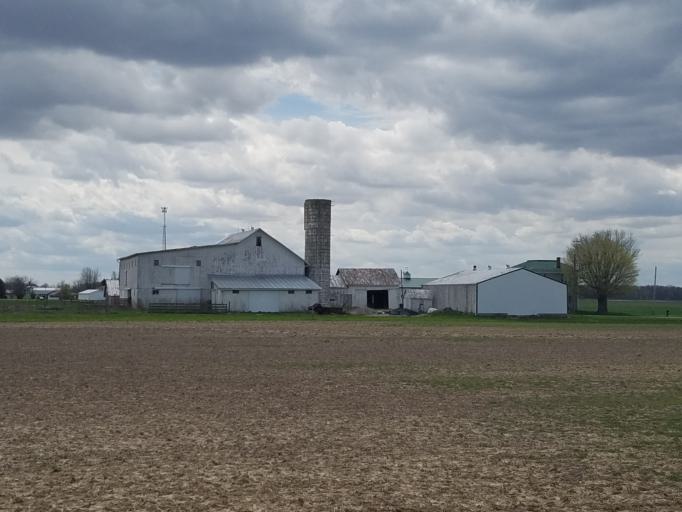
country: US
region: Ohio
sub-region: Crawford County
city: Bucyrus
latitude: 40.8442
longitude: -82.9874
